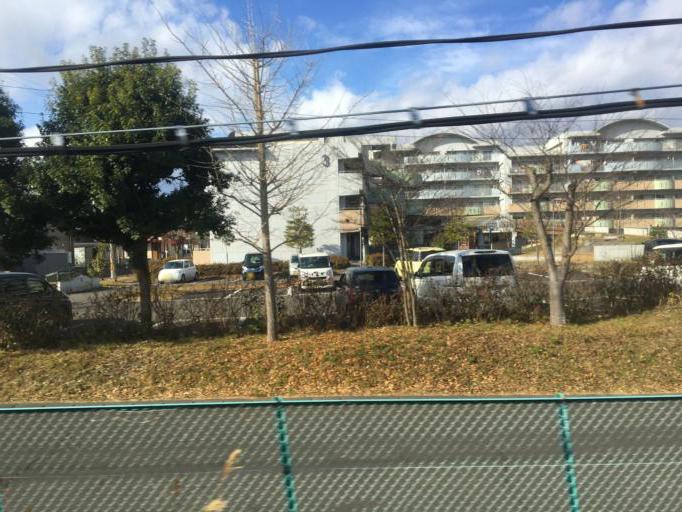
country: JP
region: Miyagi
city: Iwanuma
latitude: 38.0822
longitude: 140.8126
